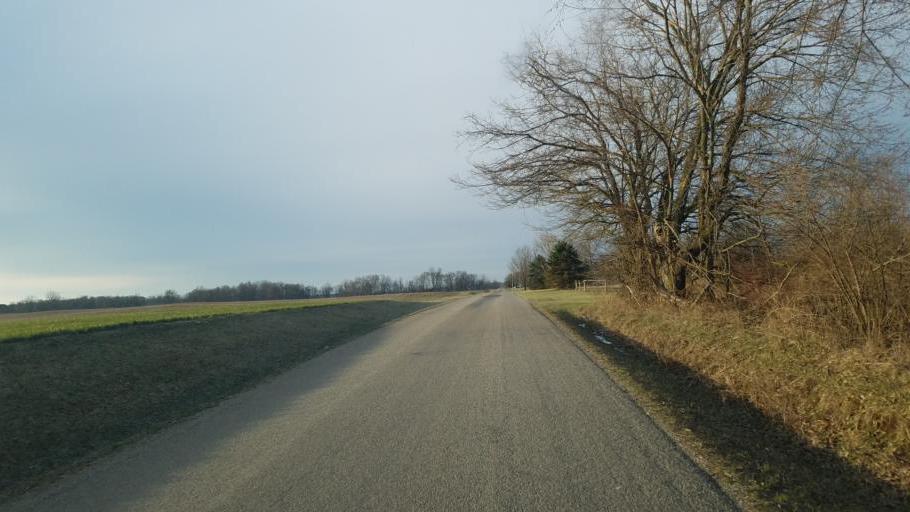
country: US
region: Ohio
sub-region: Knox County
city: Centerburg
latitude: 40.3983
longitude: -82.7407
